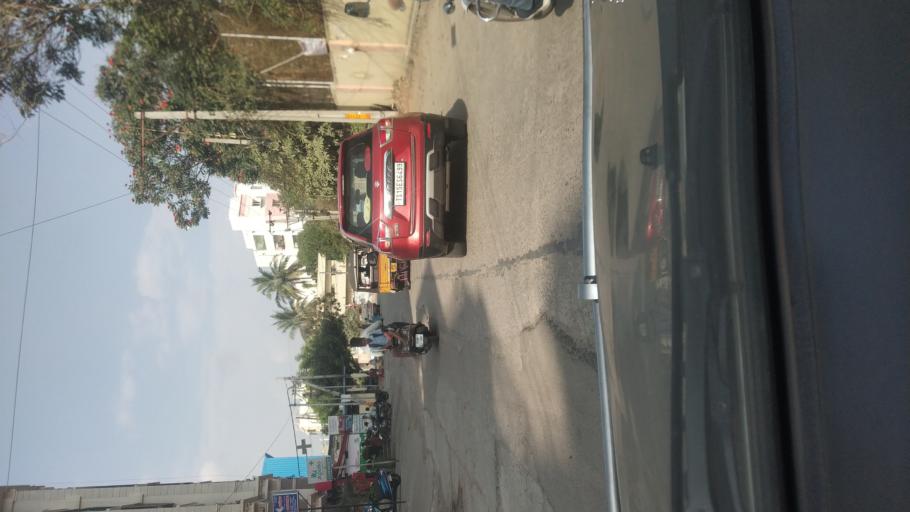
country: IN
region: Telangana
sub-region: Medak
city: Serilingampalle
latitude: 17.4889
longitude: 78.3236
